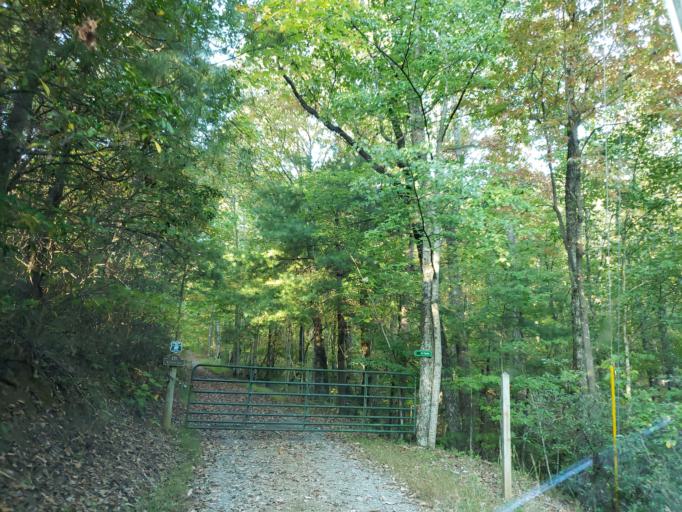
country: US
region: Georgia
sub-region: Fannin County
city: Blue Ridge
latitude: 34.6599
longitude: -84.2588
